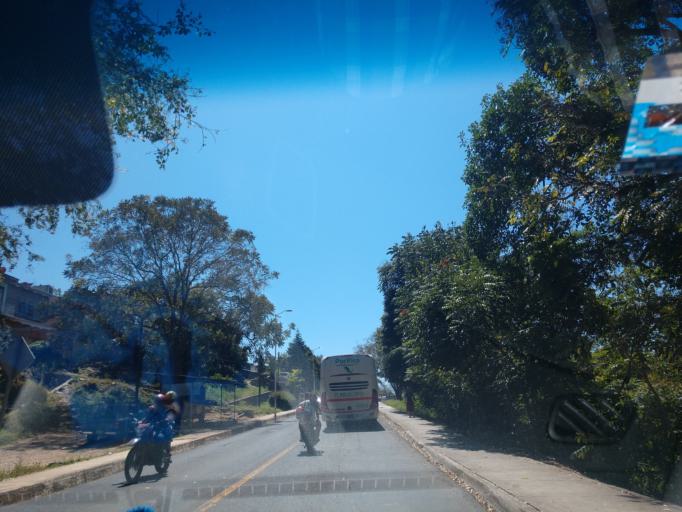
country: MX
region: Nayarit
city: Compostela
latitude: 21.2457
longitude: -104.9011
